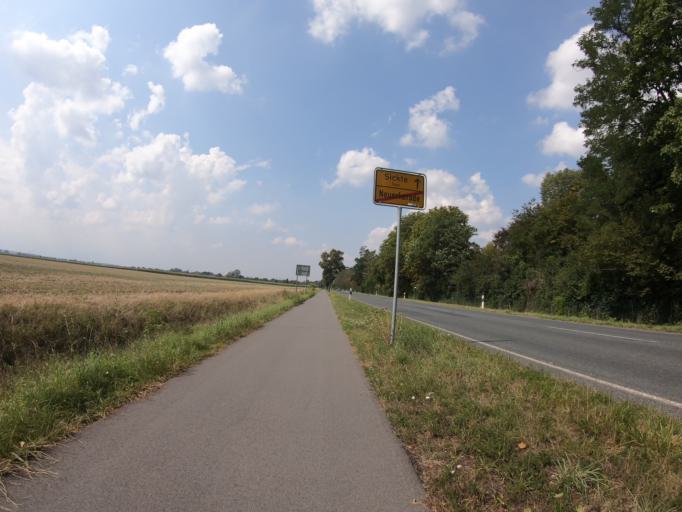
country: DE
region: Lower Saxony
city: Sickte
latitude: 52.2126
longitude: 10.6558
